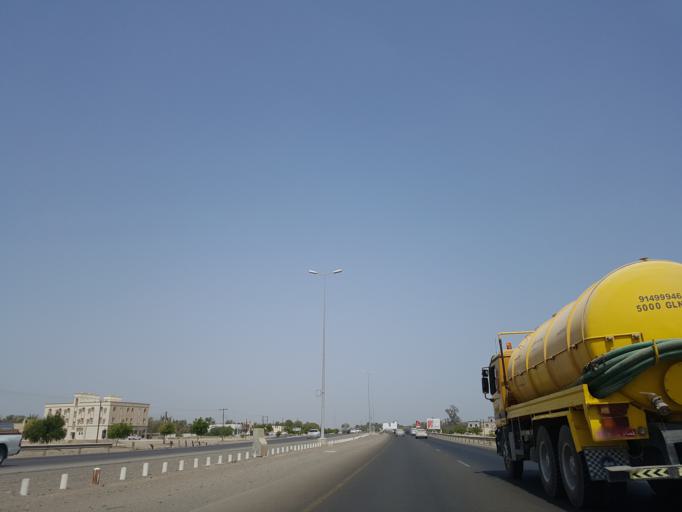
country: OM
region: Al Batinah
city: Saham
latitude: 24.1275
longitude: 56.8974
